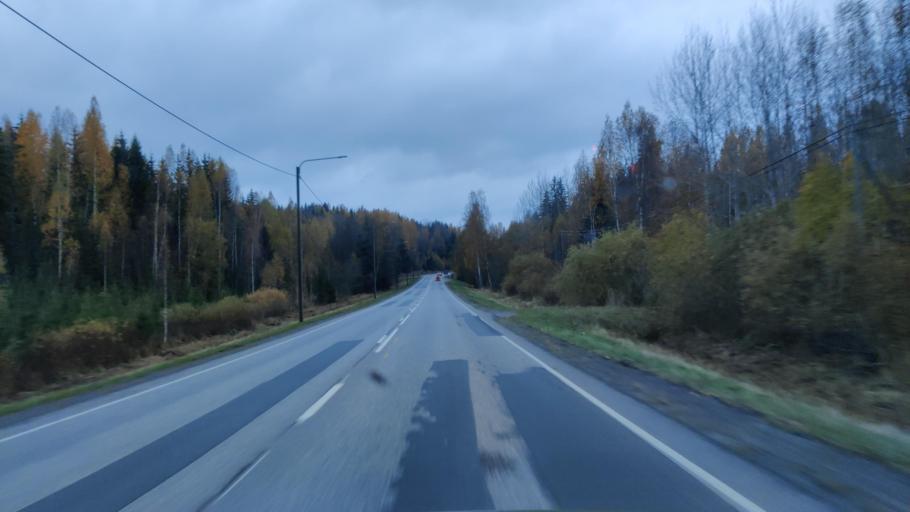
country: FI
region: Uusimaa
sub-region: Helsinki
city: Vihti
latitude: 60.3231
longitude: 24.2188
